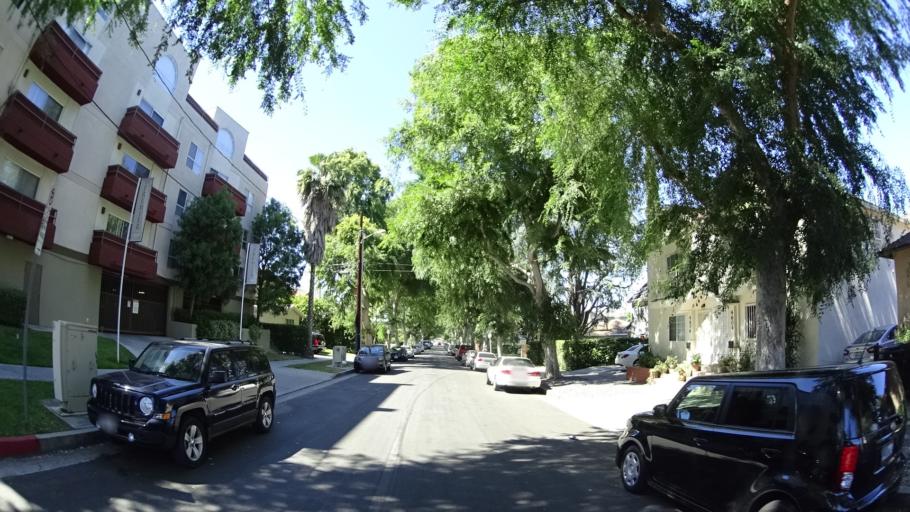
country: US
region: California
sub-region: Los Angeles County
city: Sherman Oaks
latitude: 34.1537
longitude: -118.4596
